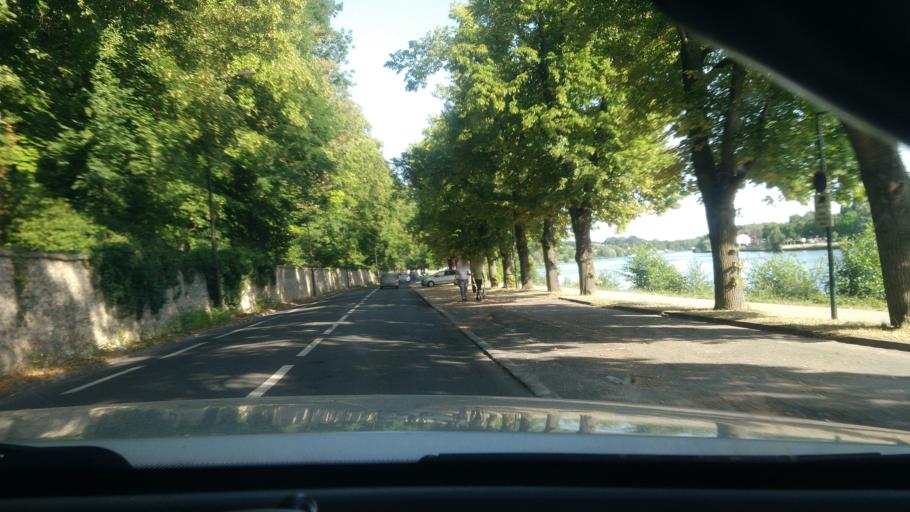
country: FR
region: Ile-de-France
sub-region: Departement de Seine-et-Marne
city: Melun
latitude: 48.5344
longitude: 2.6653
